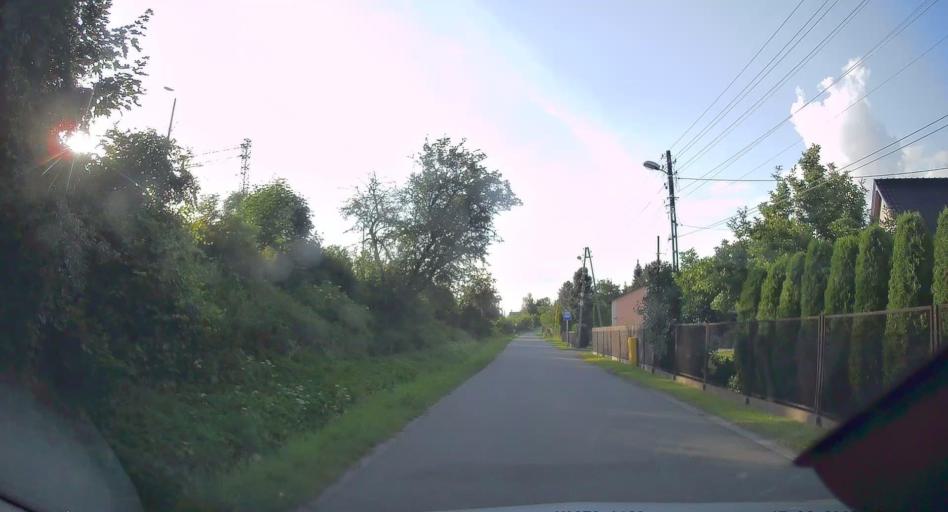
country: PL
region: Lesser Poland Voivodeship
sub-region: Powiat oswiecimski
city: Babice
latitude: 50.0707
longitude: 19.1877
